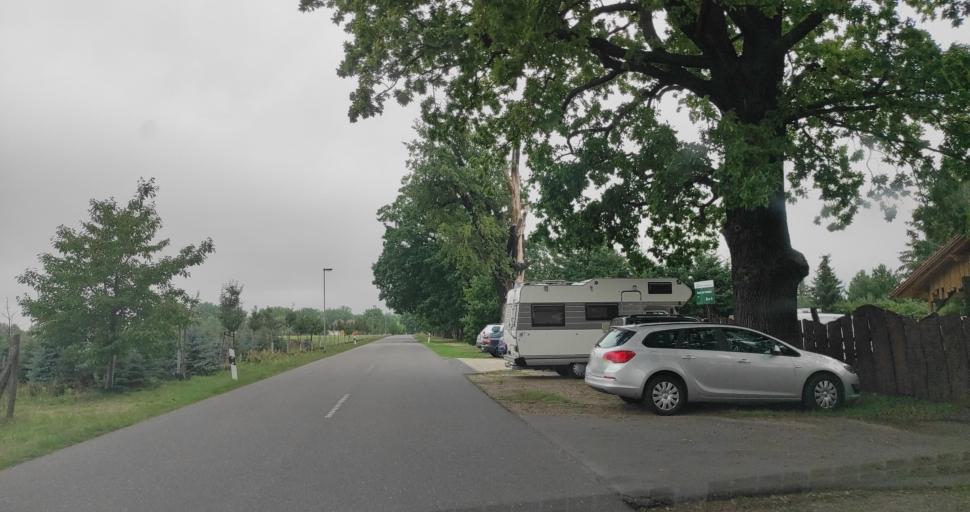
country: DE
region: Brandenburg
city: Forst
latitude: 51.7225
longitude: 14.5417
